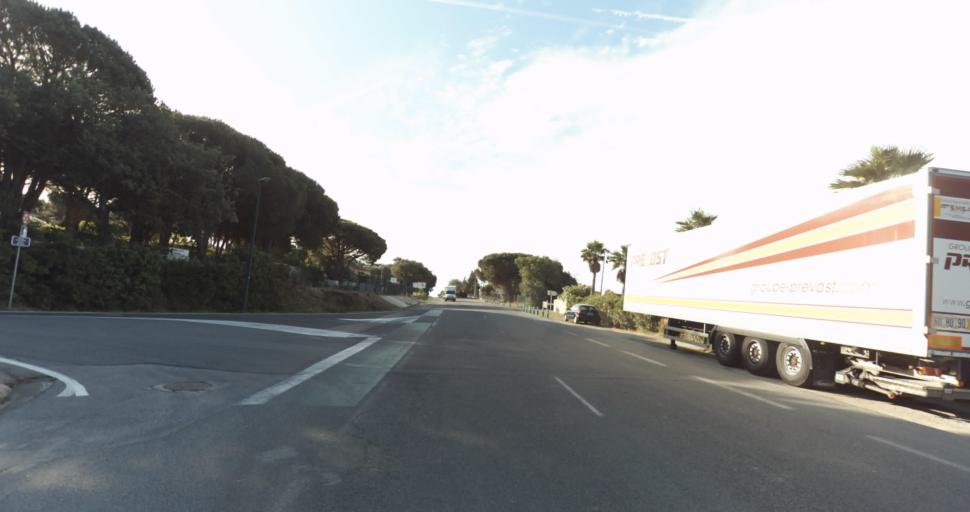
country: FR
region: Provence-Alpes-Cote d'Azur
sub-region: Departement du Var
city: Saint-Tropez
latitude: 43.2553
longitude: 6.6369
